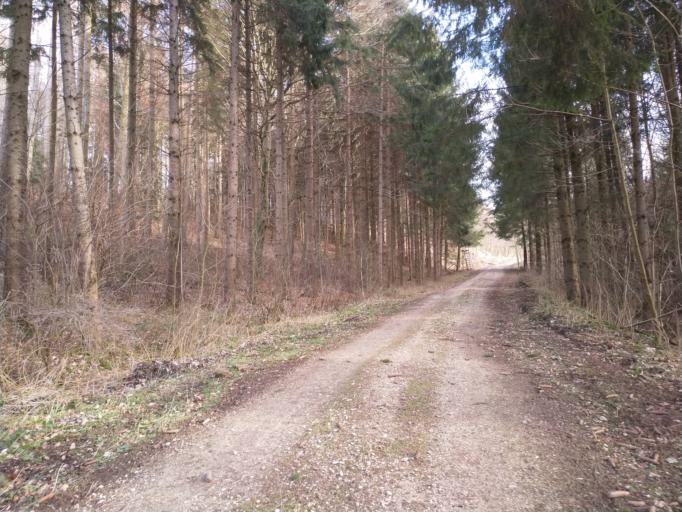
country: DE
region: Bavaria
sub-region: Swabia
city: Guenzburg
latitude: 48.4343
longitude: 10.3141
